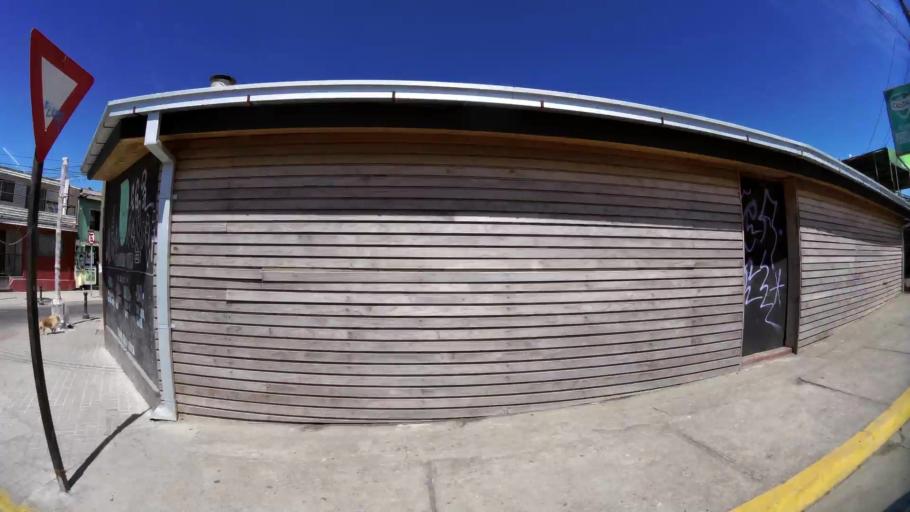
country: CL
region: Biobio
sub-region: Provincia de Concepcion
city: Penco
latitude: -36.7360
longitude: -72.9946
